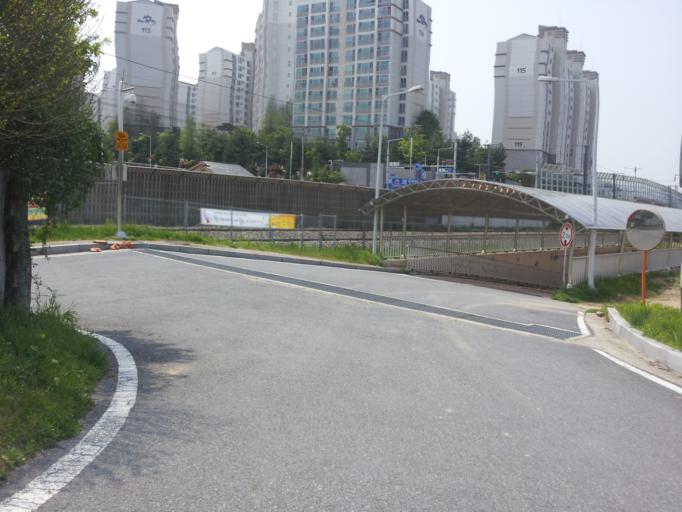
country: KR
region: Daejeon
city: Daejeon
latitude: 36.2681
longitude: 127.2750
